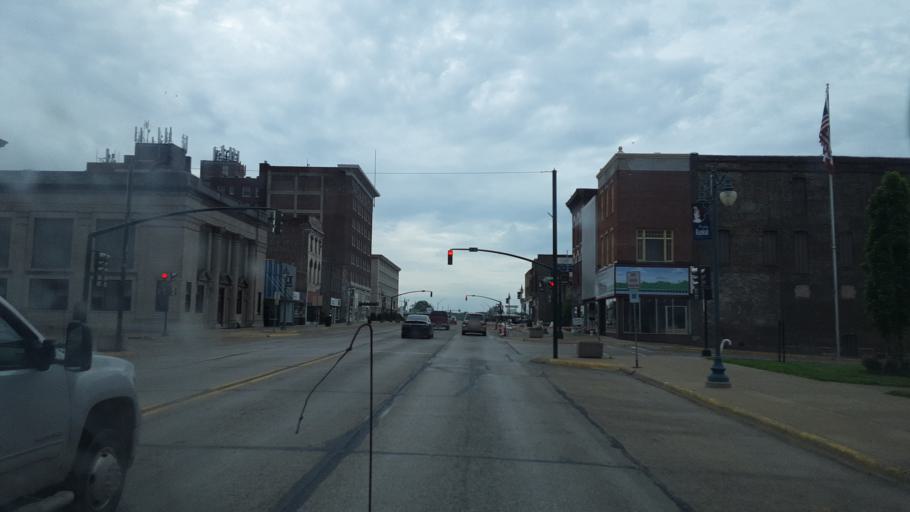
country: US
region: Iowa
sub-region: Lee County
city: Keokuk
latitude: 40.3961
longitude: -91.3837
